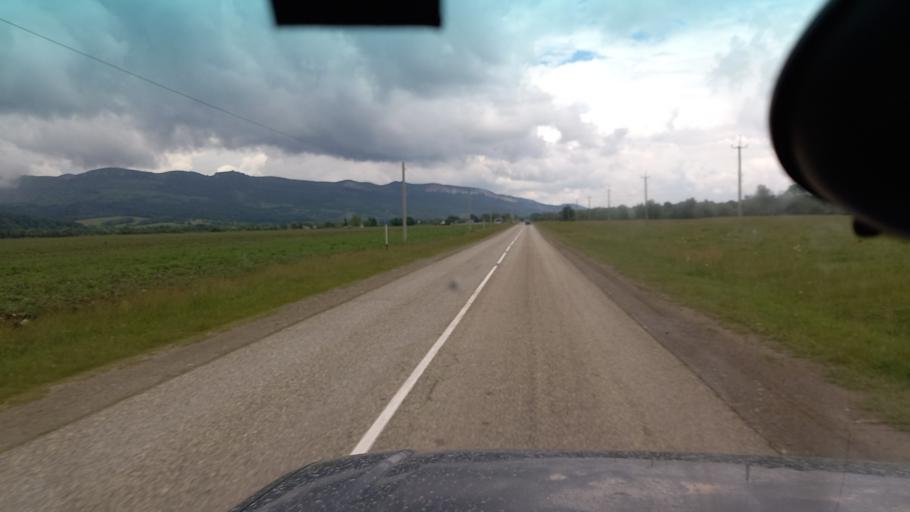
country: RU
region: Krasnodarskiy
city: Psebay
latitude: 44.0778
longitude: 40.7800
